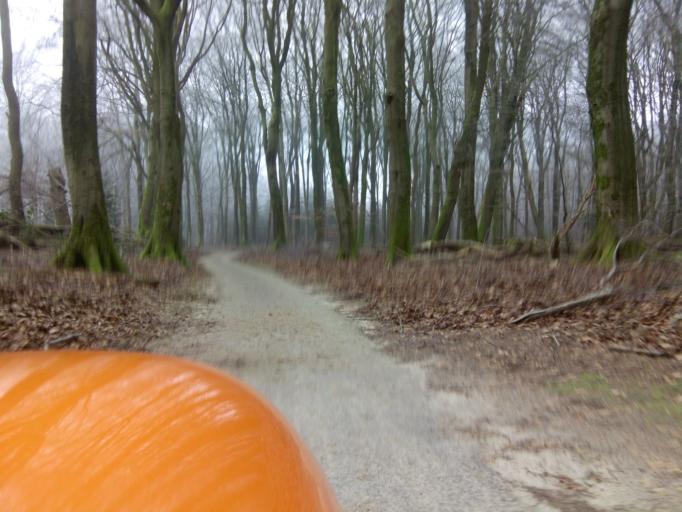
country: NL
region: Gelderland
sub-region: Gemeente Barneveld
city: Garderen
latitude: 52.2623
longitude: 5.6834
